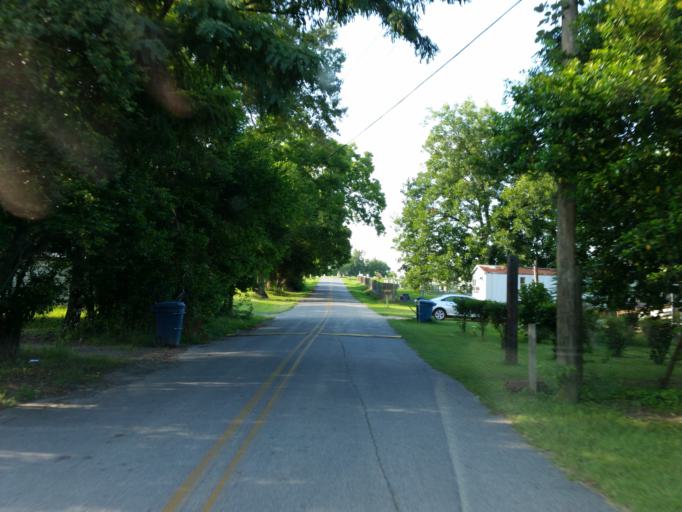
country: US
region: Georgia
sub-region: Dooly County
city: Vienna
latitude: 32.0960
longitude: -83.7964
